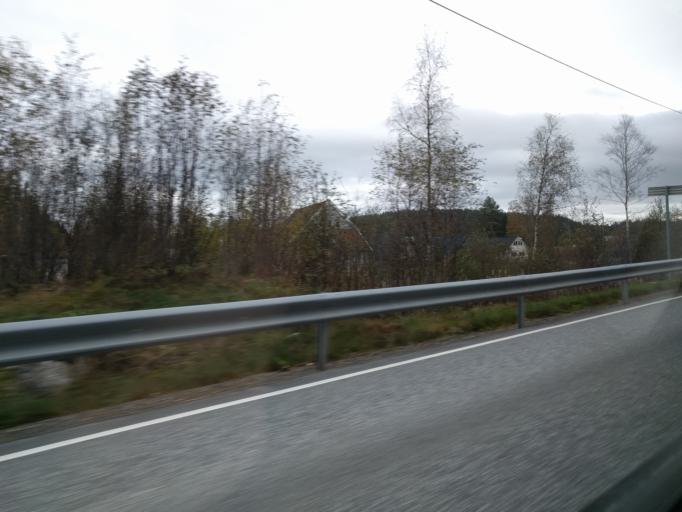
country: NO
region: Aust-Agder
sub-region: Iveland
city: Birketveit
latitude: 58.3821
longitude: 7.7458
